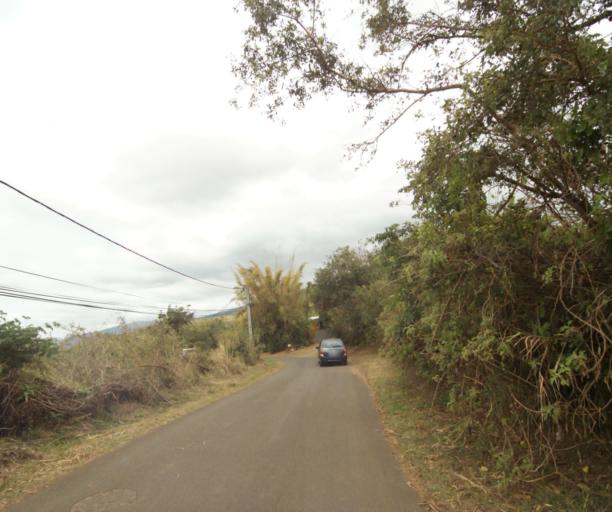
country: RE
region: Reunion
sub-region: Reunion
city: Saint-Paul
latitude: -21.0294
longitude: 55.2992
